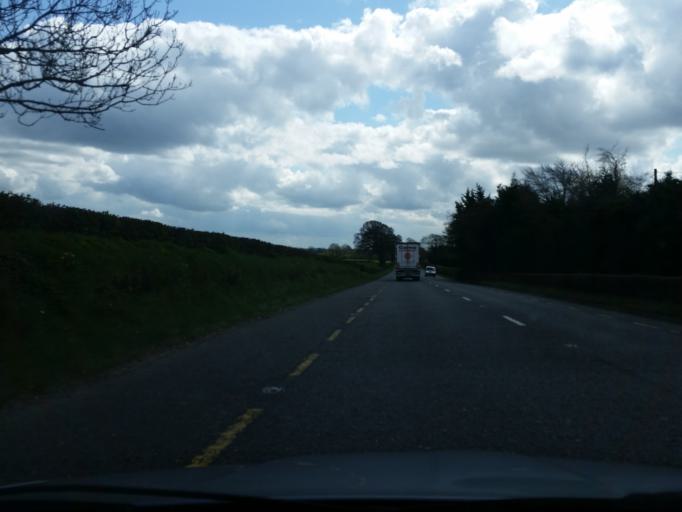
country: IE
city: Kentstown
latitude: 53.6123
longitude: -6.4785
